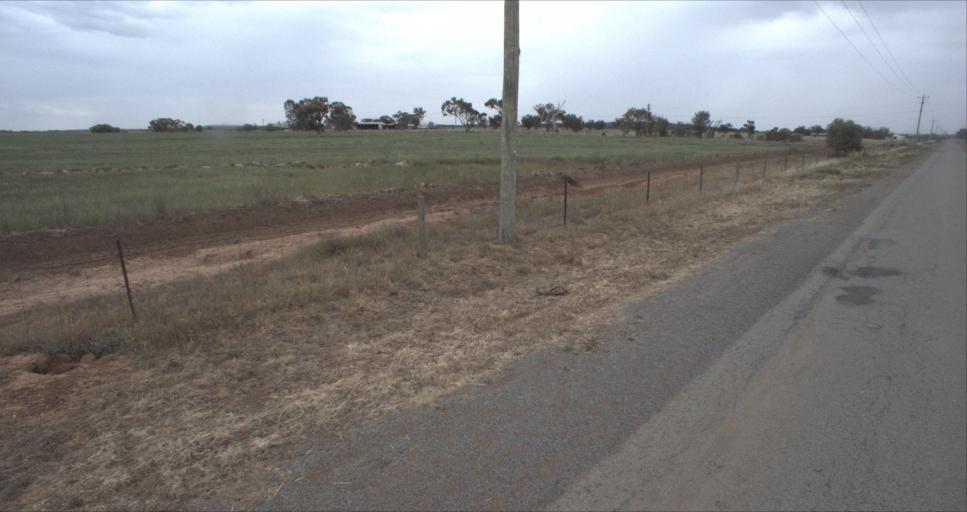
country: AU
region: New South Wales
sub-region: Leeton
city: Leeton
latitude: -34.4160
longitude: 146.3394
